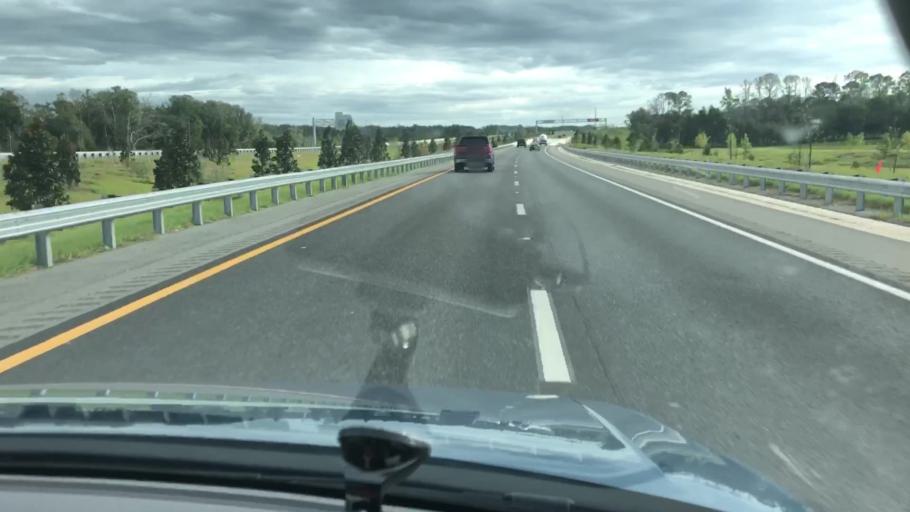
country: US
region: Florida
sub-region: Orange County
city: Zellwood
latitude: 28.7359
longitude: -81.5643
